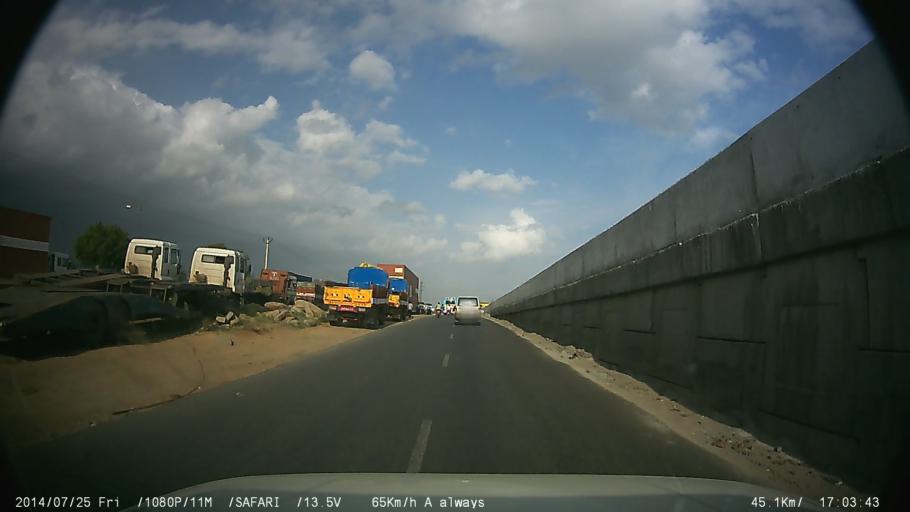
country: IN
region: Tamil Nadu
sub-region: Krishnagiri
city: Hosur
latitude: 12.7167
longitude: 77.8798
